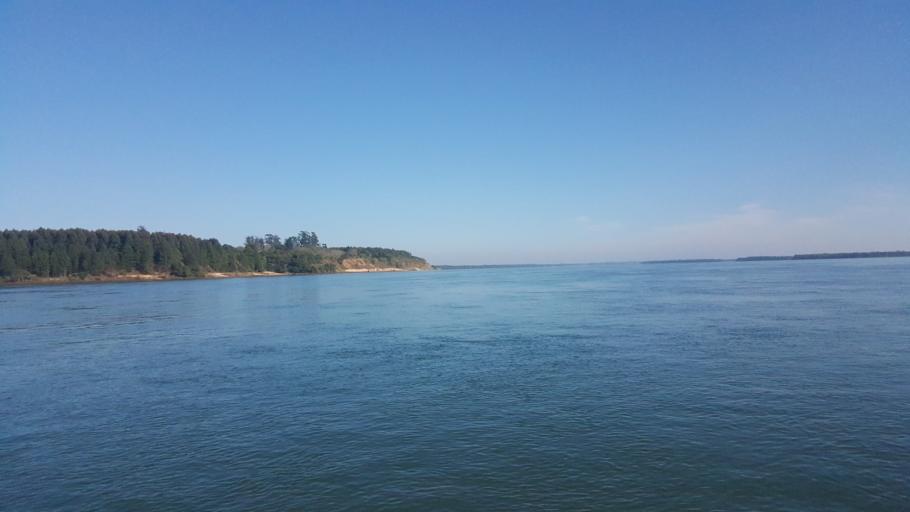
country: AR
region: Corrientes
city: Ituzaingo
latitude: -27.6027
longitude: -56.8575
